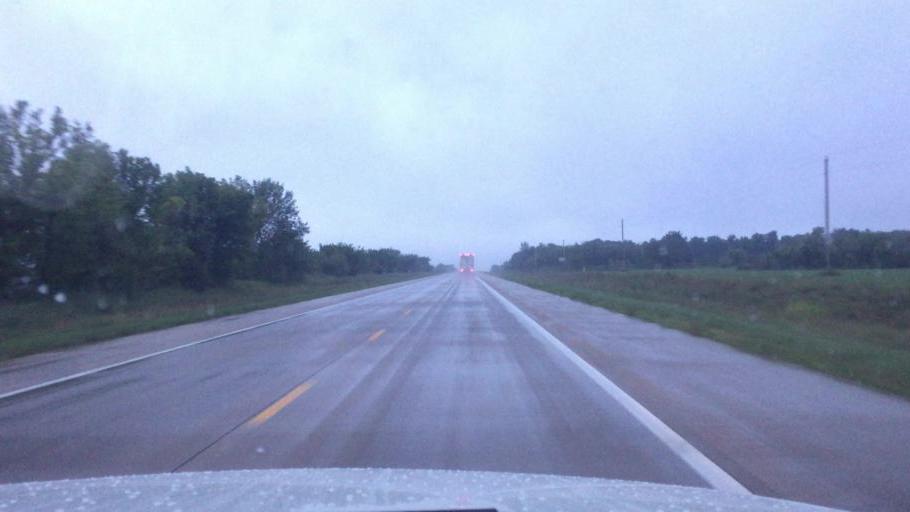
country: US
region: Kansas
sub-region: Neosho County
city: Chanute
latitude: 37.5500
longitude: -95.4708
